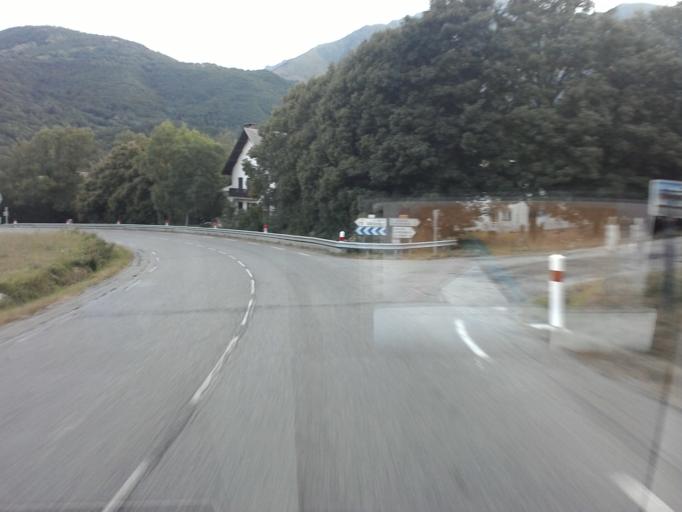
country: FR
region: Provence-Alpes-Cote d'Azur
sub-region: Departement des Hautes-Alpes
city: Saint-Bonnet-en-Champsaur
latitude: 44.7713
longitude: 6.0247
